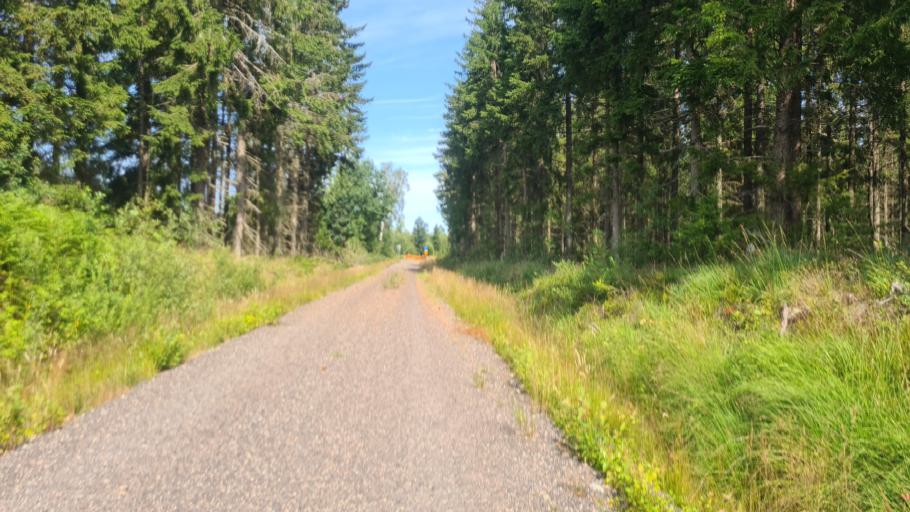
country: SE
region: Kronoberg
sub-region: Ljungby Kommun
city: Lagan
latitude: 56.9829
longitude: 13.9450
